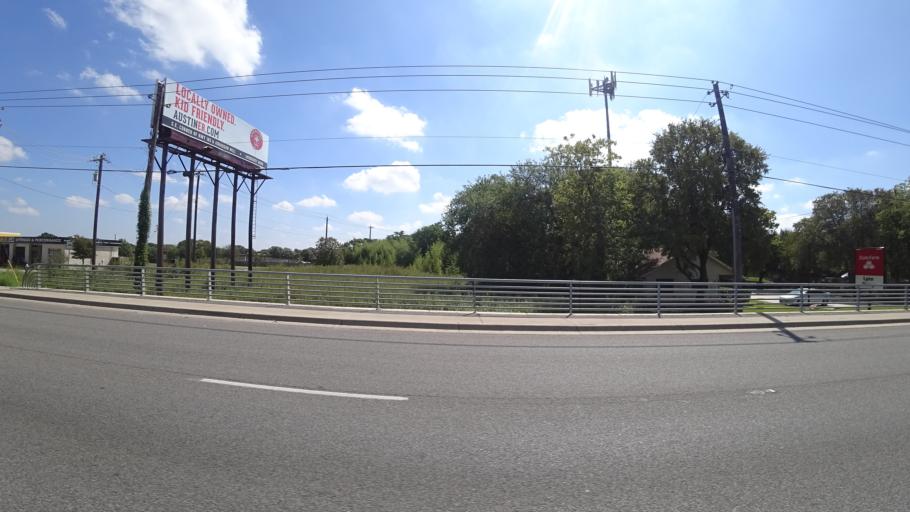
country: US
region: Texas
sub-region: Williamson County
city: Anderson Mill
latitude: 30.4720
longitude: -97.7842
